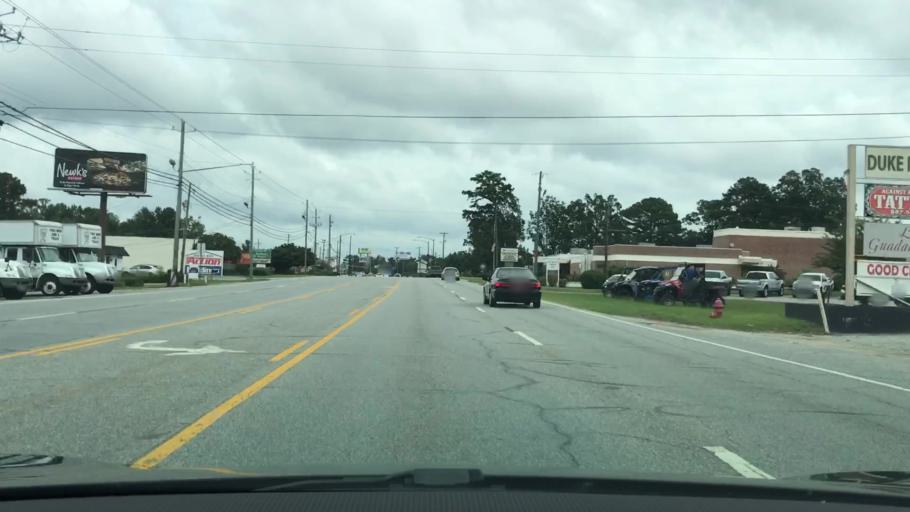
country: US
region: Alabama
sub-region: Lee County
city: Auburn
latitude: 32.6275
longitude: -85.4409
